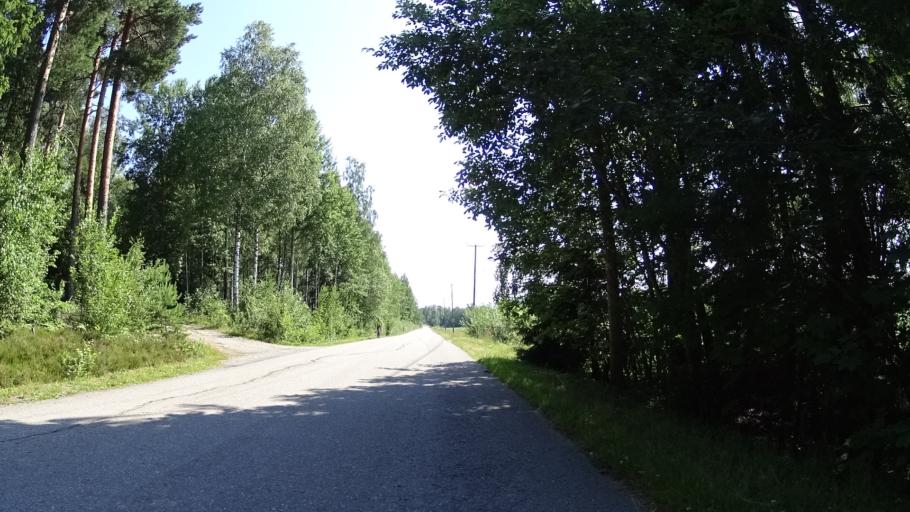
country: FI
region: Uusimaa
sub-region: Helsinki
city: Jaervenpaeae
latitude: 60.4470
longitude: 25.0890
